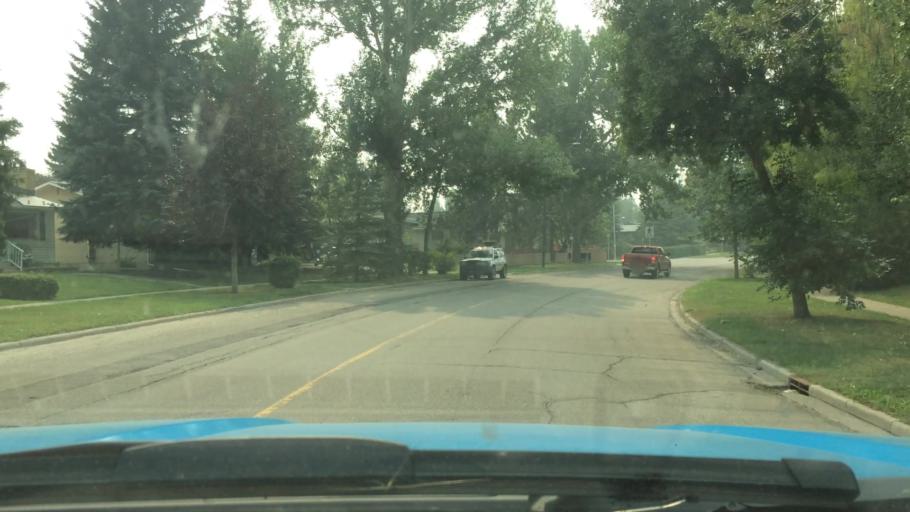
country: CA
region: Alberta
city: Calgary
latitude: 51.0963
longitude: -114.1256
